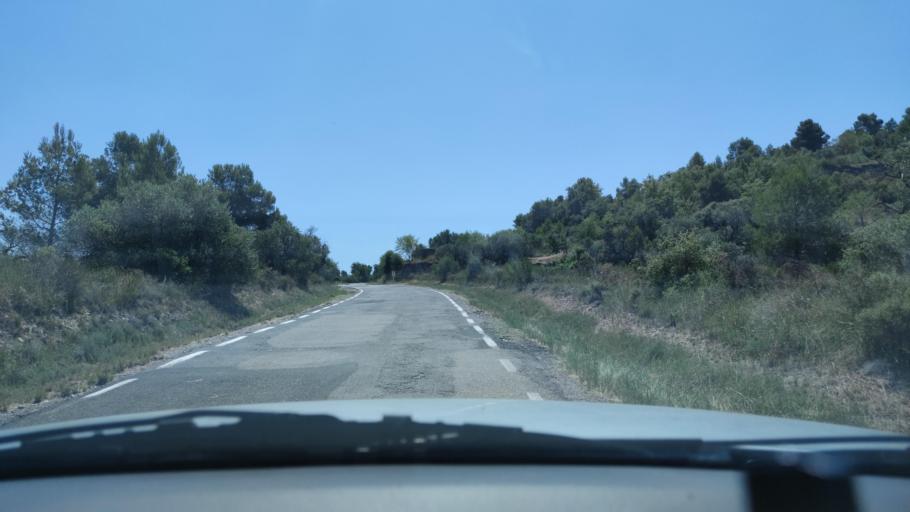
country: ES
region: Catalonia
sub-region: Provincia de Lleida
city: Fulleda
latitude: 41.4800
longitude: 1.0171
